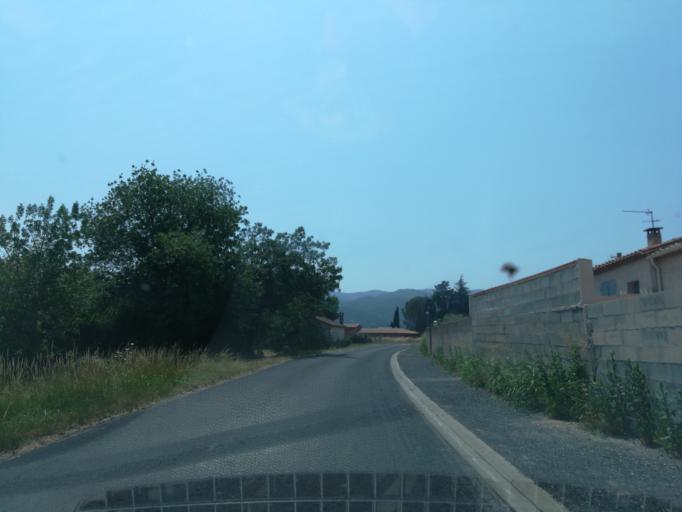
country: FR
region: Languedoc-Roussillon
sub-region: Departement des Pyrenees-Orientales
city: Maureillas-las-Illas
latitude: 42.4933
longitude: 2.8021
